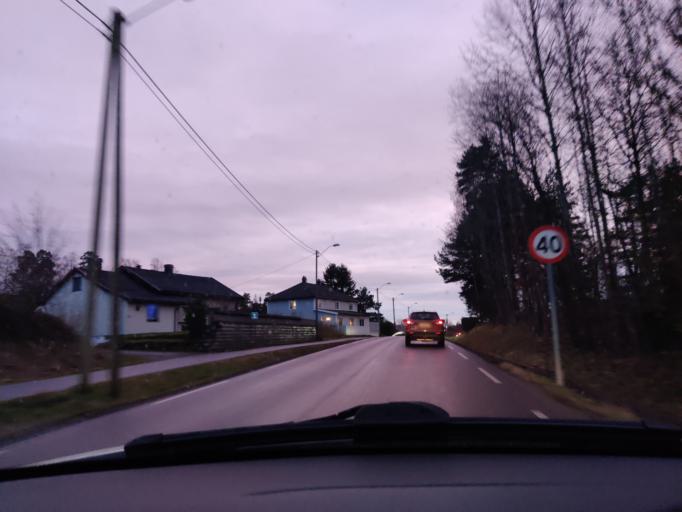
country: NO
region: Vestfold
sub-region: Tonsberg
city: Sem
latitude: 59.2630
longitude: 10.3632
